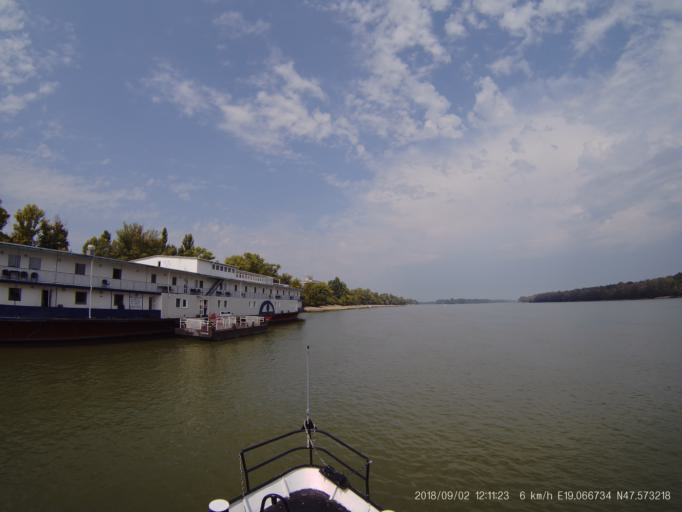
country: HU
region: Budapest
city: Budapest IV. keruelet
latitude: 47.5731
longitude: 19.0668
